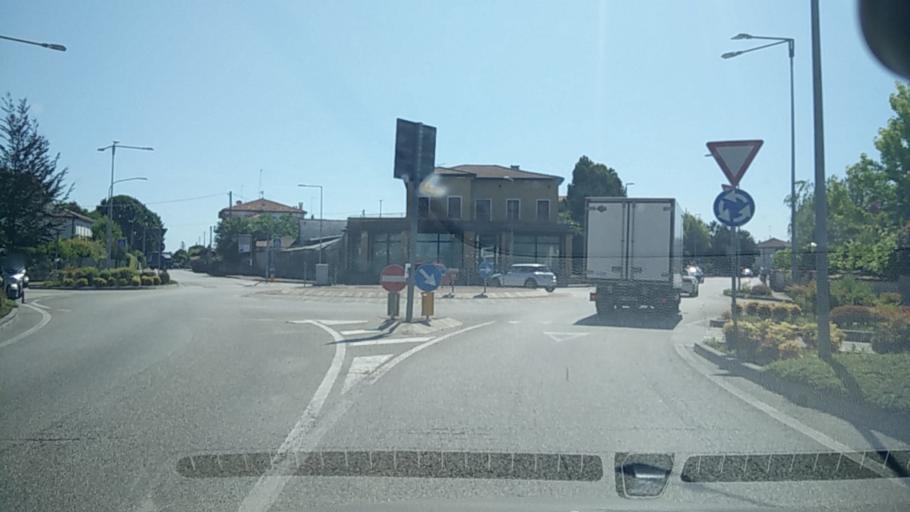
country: IT
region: Veneto
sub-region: Provincia di Venezia
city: Camponogara
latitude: 45.3825
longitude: 12.0779
